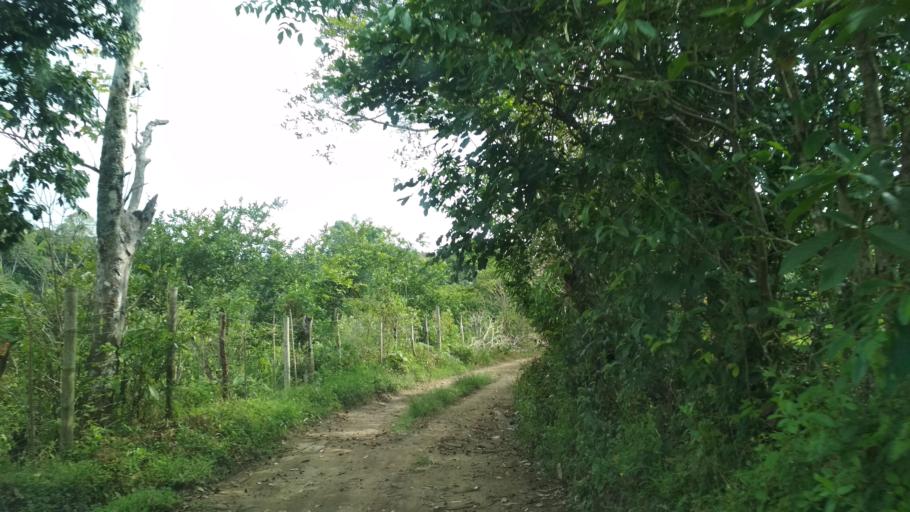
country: CO
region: Cauca
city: Lopez
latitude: 2.4041
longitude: -76.7134
